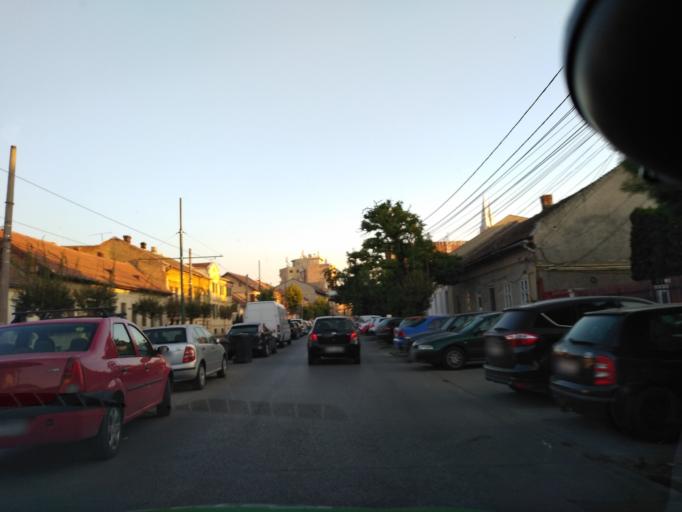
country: RO
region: Timis
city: Timisoara
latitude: 45.7391
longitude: 21.2251
